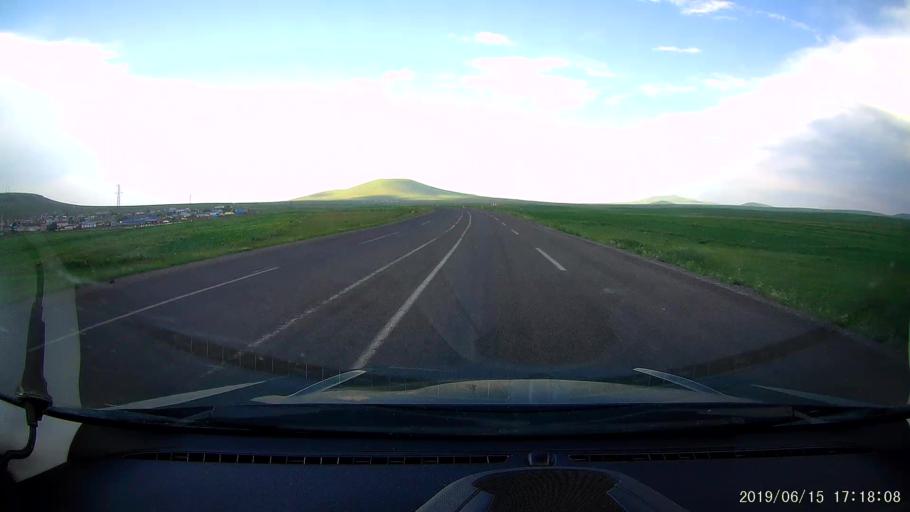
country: TR
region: Kars
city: Kars
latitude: 40.6134
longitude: 43.2517
